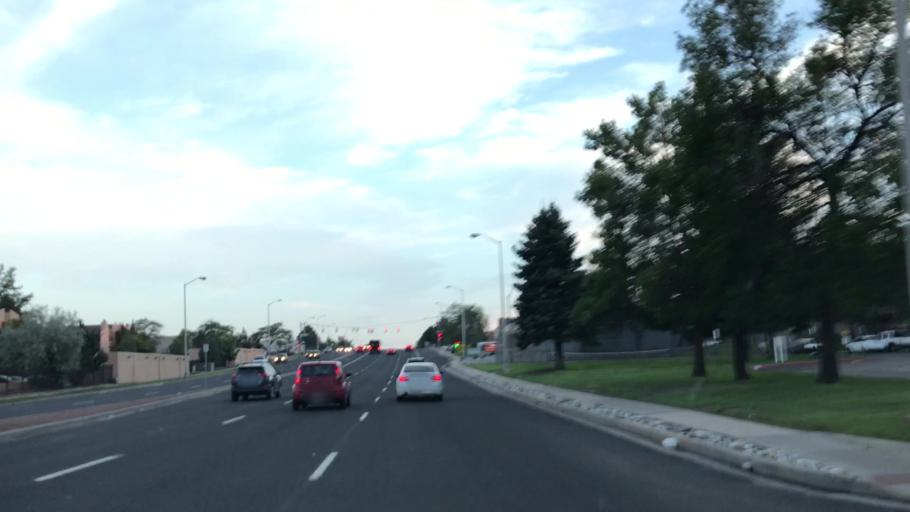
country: US
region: Colorado
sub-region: El Paso County
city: Cimarron Hills
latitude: 38.8844
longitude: -104.7571
